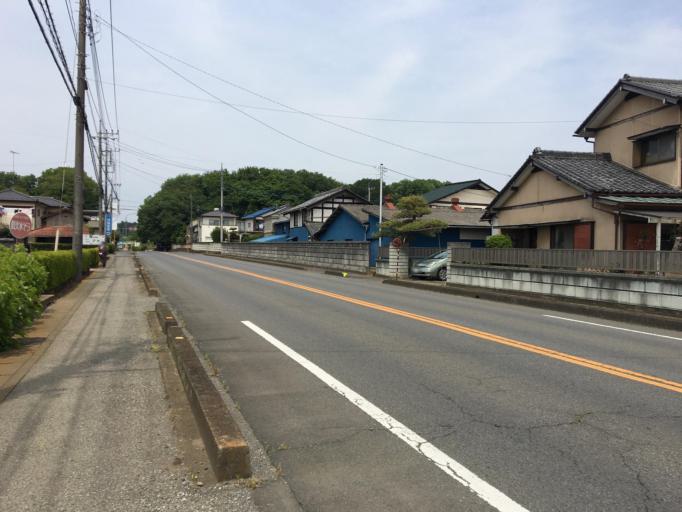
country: JP
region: Tochigi
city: Oyama
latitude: 36.3539
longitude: 139.8134
